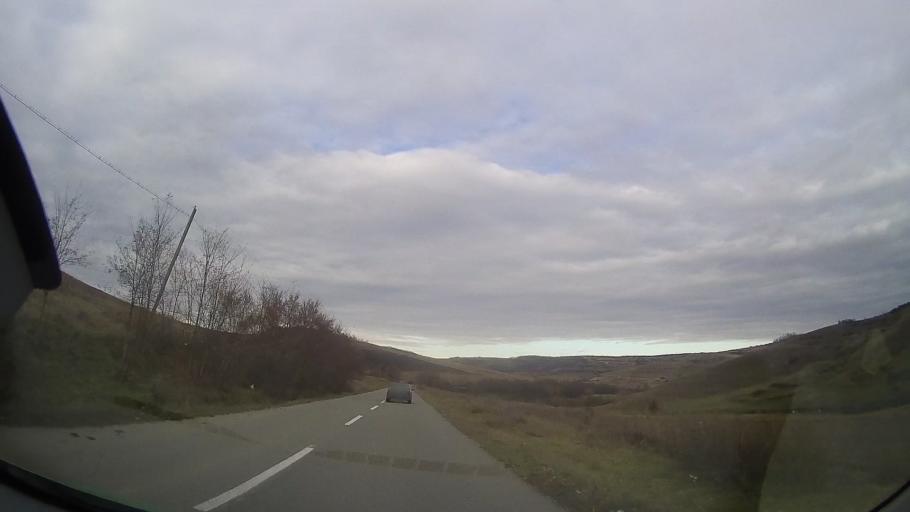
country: RO
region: Bistrita-Nasaud
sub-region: Comuna Milas
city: Milas
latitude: 46.8286
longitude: 24.4487
